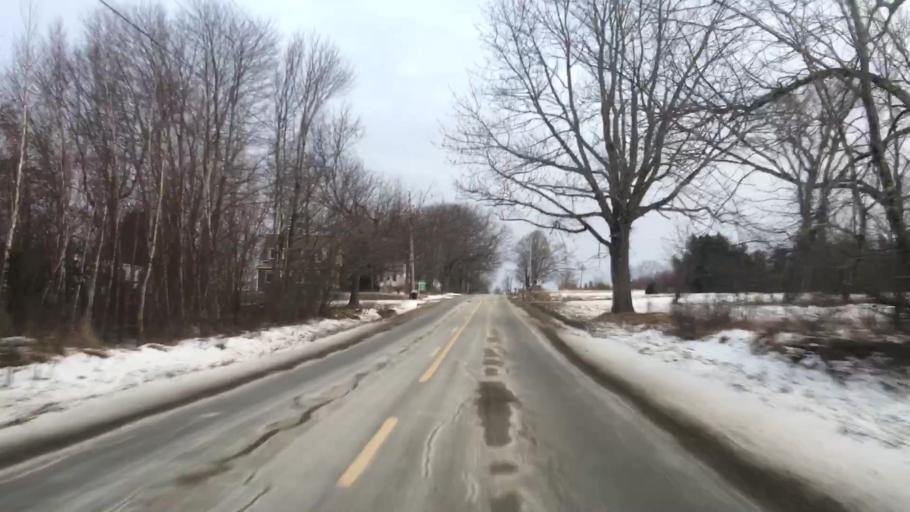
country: US
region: Maine
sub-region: Hancock County
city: Franklin
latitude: 44.7065
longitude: -68.3403
